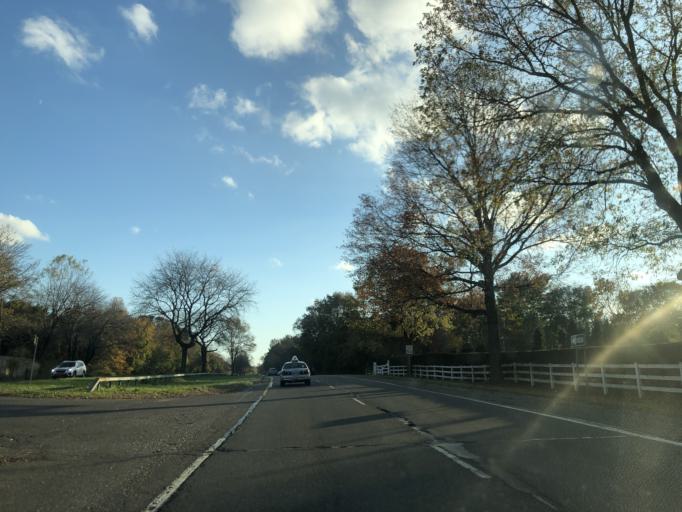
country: US
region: New York
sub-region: Nassau County
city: Glen Head
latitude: 40.8255
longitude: -73.6247
